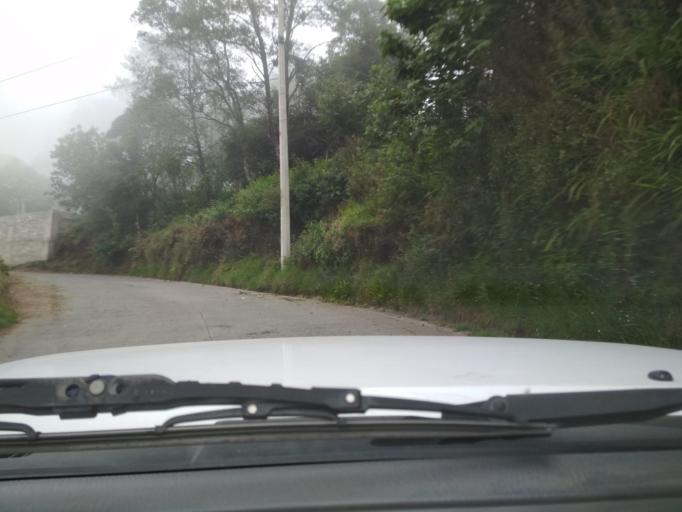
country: MX
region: Veracruz
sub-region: La Perla
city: Chilapa
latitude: 18.9744
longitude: -97.1584
